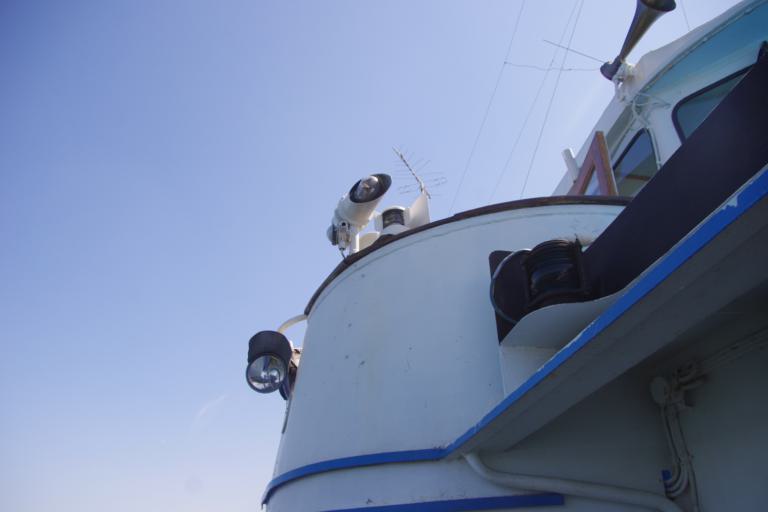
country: RU
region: Samara
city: Rozhdestveno
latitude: 53.2052
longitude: 50.0786
